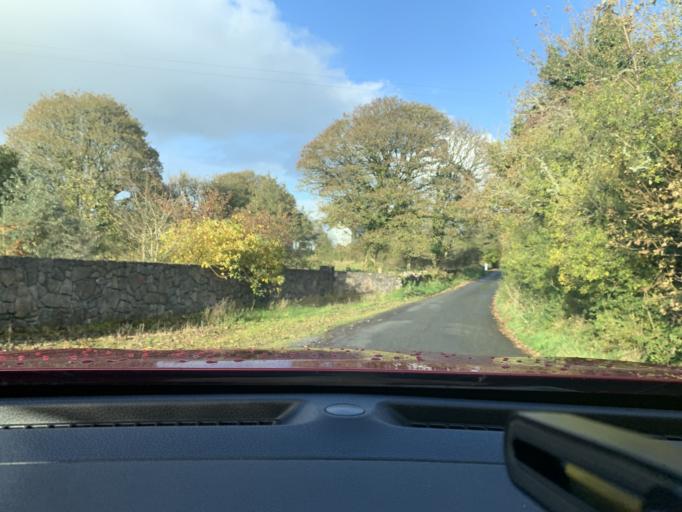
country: IE
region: Connaught
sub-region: Sligo
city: Ballymote
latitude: 54.1000
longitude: -8.4357
